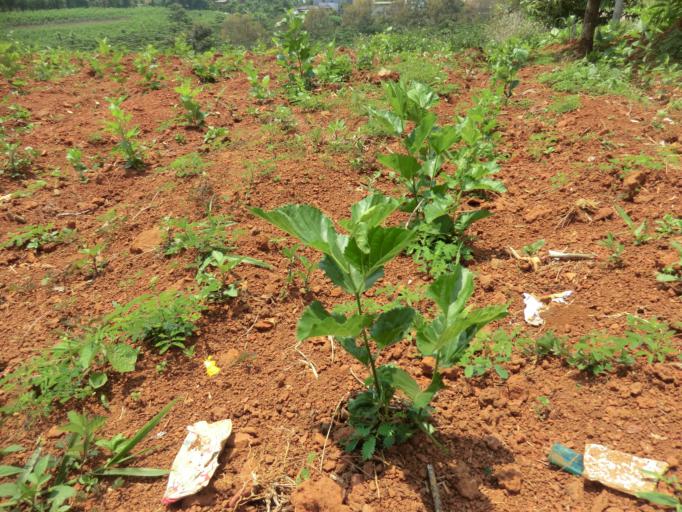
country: VN
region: Lam Dong
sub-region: Thanh Pho Bao Loc
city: Bao Loc
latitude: 11.5911
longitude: 107.7871
